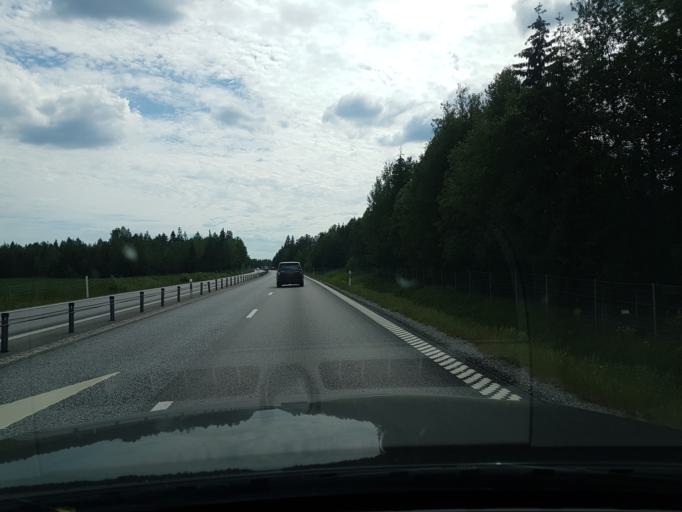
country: SE
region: Stockholm
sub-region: Osterakers Kommun
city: Akersberga
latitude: 59.6067
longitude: 18.2787
